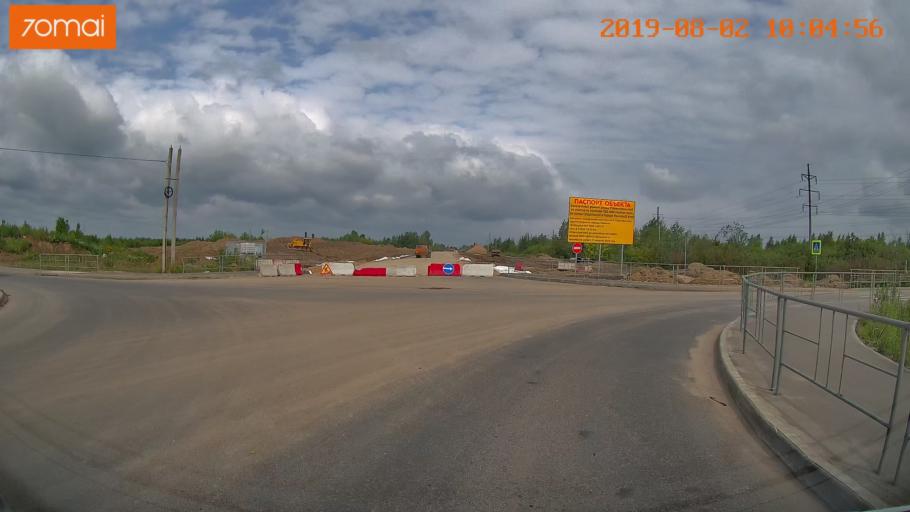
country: RU
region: Ivanovo
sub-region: Gorod Ivanovo
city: Ivanovo
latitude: 56.9762
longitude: 40.9218
